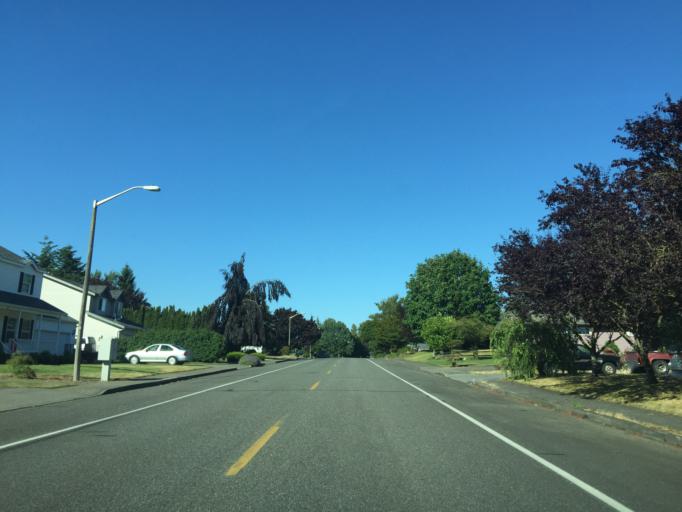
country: US
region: Washington
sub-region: Whatcom County
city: Lynden
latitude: 48.9550
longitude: -122.4393
